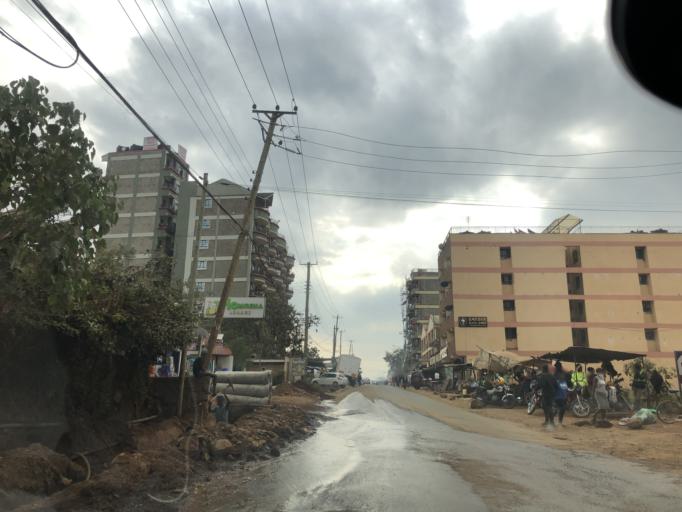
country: KE
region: Kiambu
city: Kiambu
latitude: -1.2106
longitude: 36.8859
